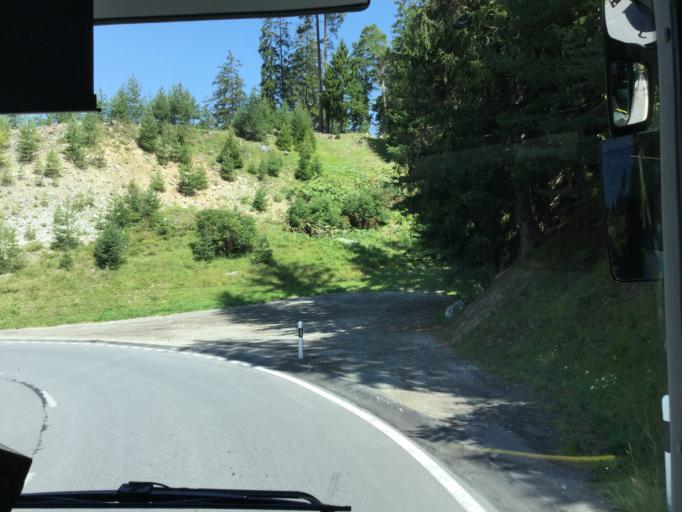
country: CH
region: Grisons
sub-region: Albula District
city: Tiefencastel
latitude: 46.6421
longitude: 9.5856
